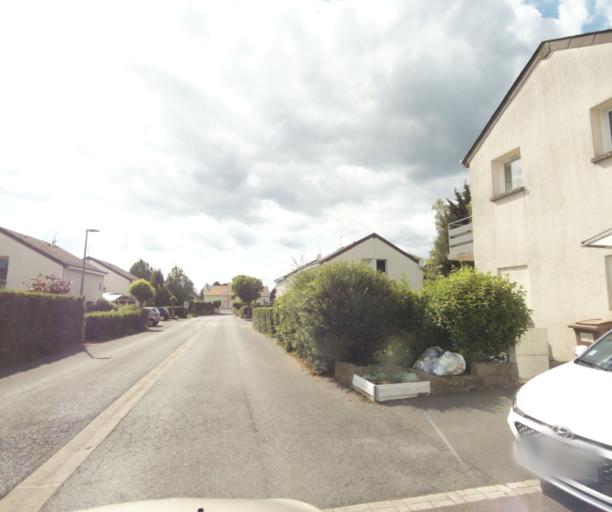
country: FR
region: Champagne-Ardenne
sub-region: Departement des Ardennes
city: Montcy-Notre-Dame
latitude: 49.7606
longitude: 4.7462
